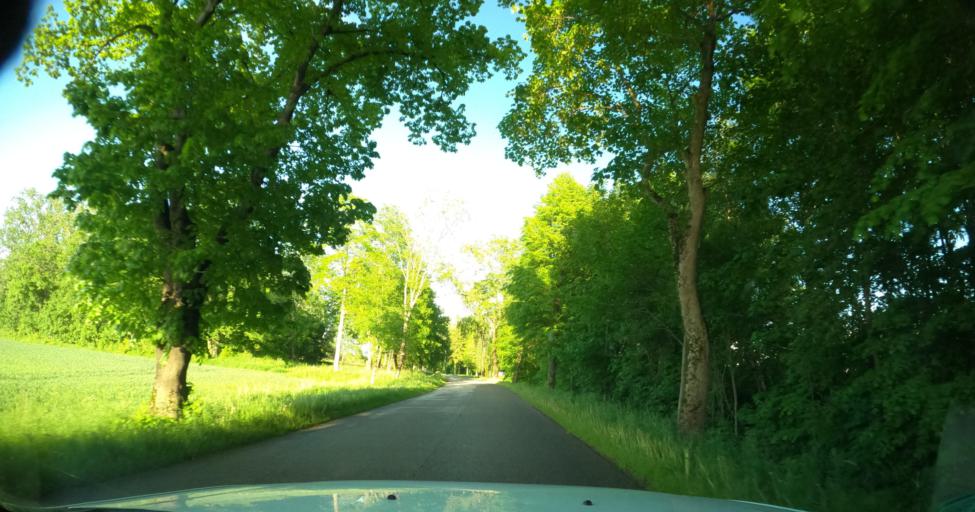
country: PL
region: Warmian-Masurian Voivodeship
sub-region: Powiat braniewski
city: Pieniezno
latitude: 54.2544
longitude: 19.9789
